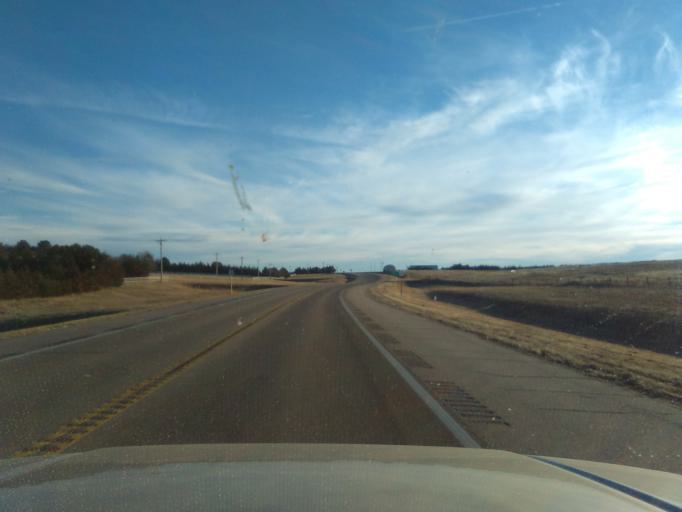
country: US
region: Kansas
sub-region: Logan County
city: Oakley
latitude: 39.1829
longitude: -100.8700
